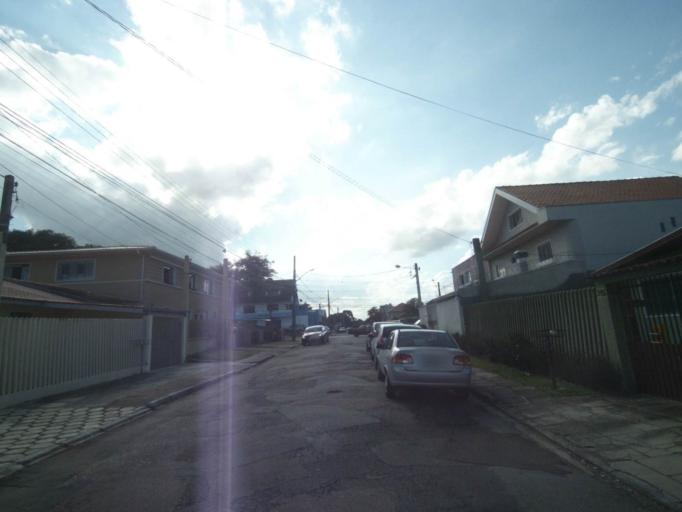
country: BR
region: Parana
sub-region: Pinhais
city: Pinhais
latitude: -25.4381
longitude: -49.2190
